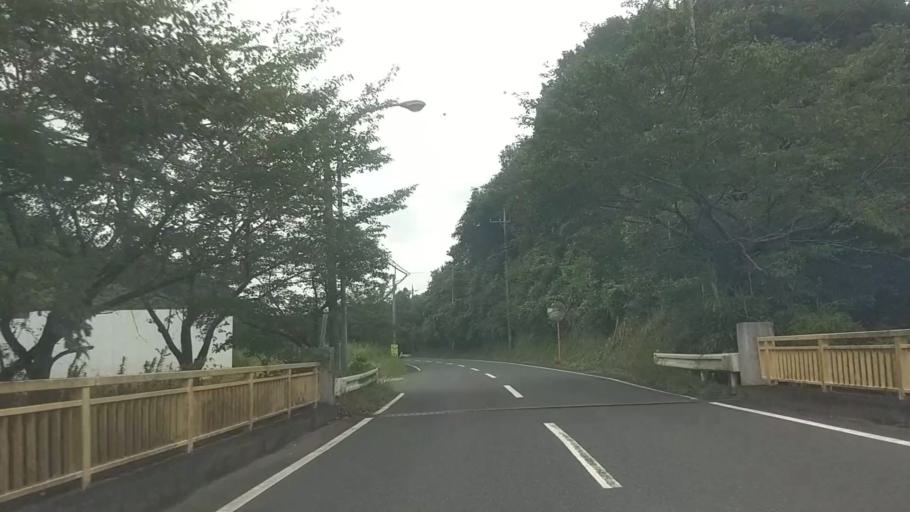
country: JP
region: Chiba
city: Kimitsu
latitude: 35.2239
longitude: 139.9521
